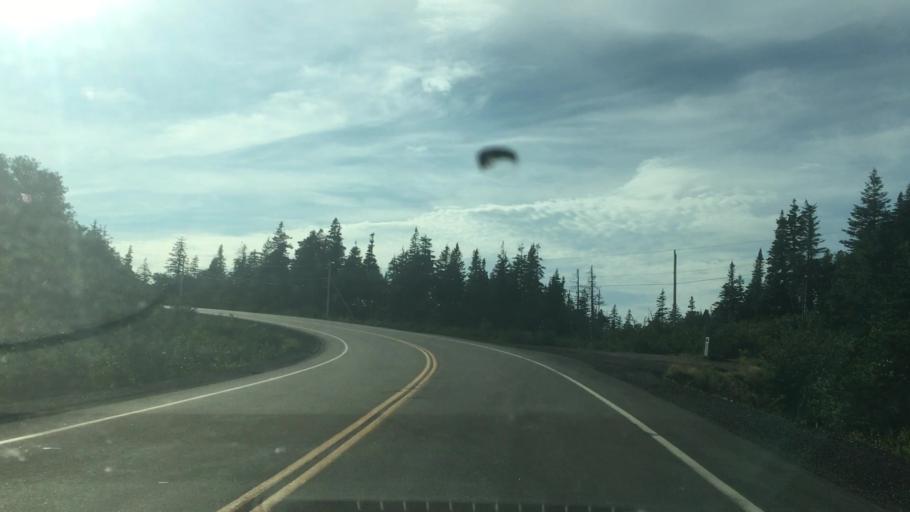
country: CA
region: Nova Scotia
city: Sydney Mines
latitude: 46.8241
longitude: -60.6580
